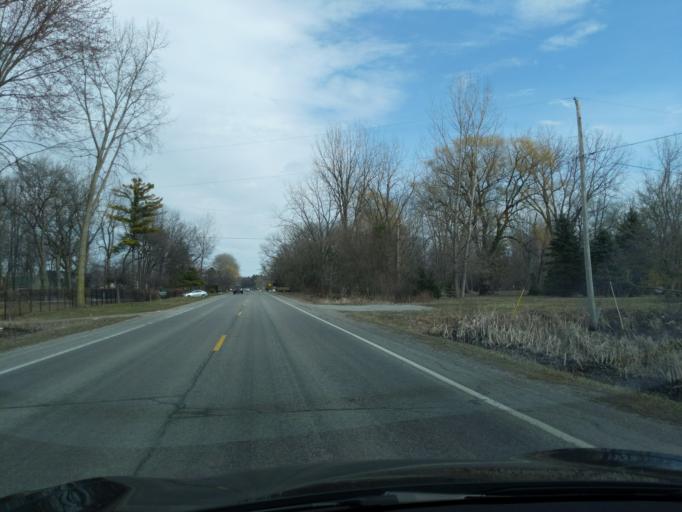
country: US
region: Michigan
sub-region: Bay County
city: Bay City
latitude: 43.6673
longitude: -83.9203
